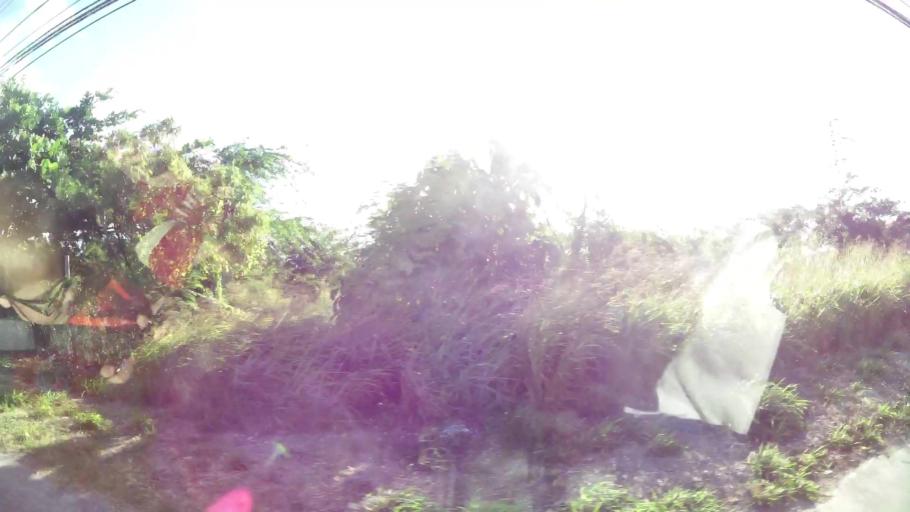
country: AG
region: Saint George
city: Piggotts
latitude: 17.1218
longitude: -61.8028
